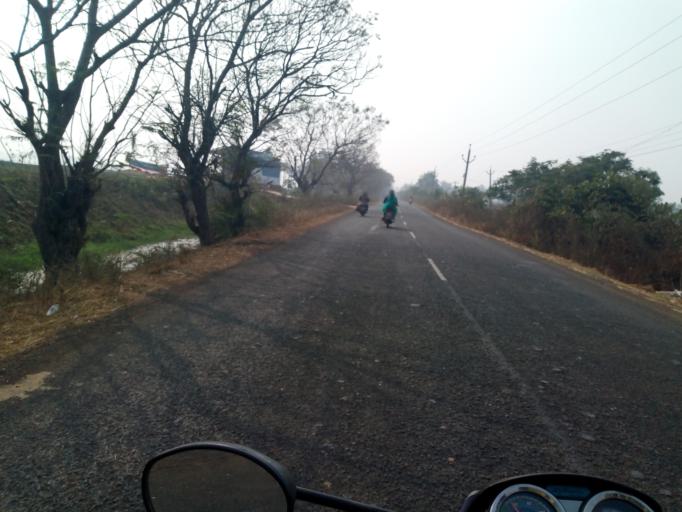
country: IN
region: Andhra Pradesh
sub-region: West Godavari
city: Tadepallegudem
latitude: 16.7896
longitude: 81.4190
